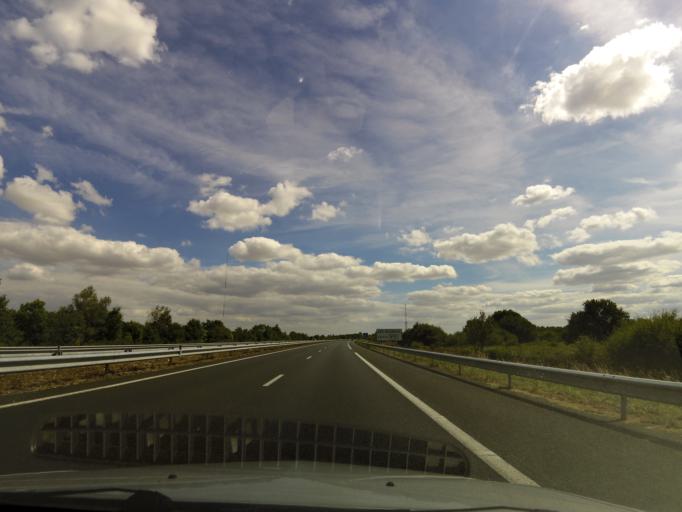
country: FR
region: Pays de la Loire
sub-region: Departement de la Vendee
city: Chauche
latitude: 46.8337
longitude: -1.2277
